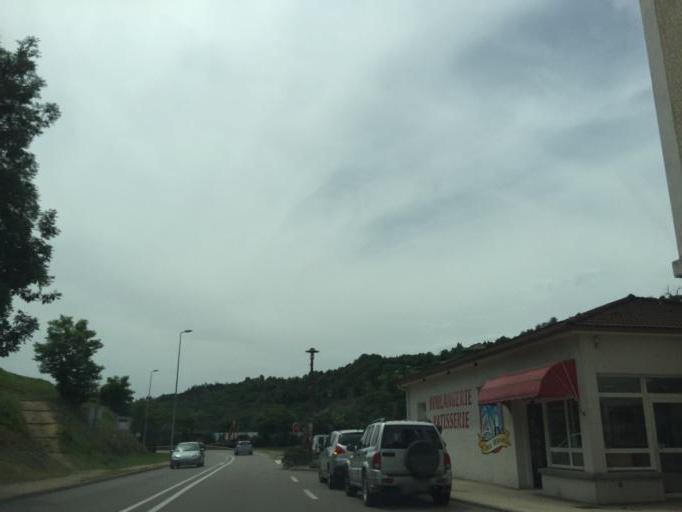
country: FR
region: Rhone-Alpes
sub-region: Departement de l'Ardeche
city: Saint-Marcel-les-Annonay
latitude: 45.2846
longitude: 4.6315
